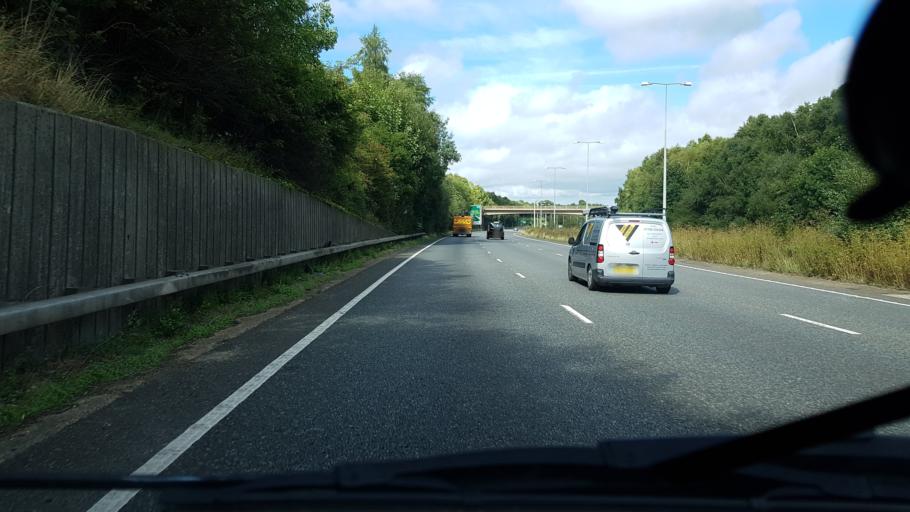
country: GB
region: England
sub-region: West Sussex
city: Broadfield
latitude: 51.0810
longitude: -0.2028
